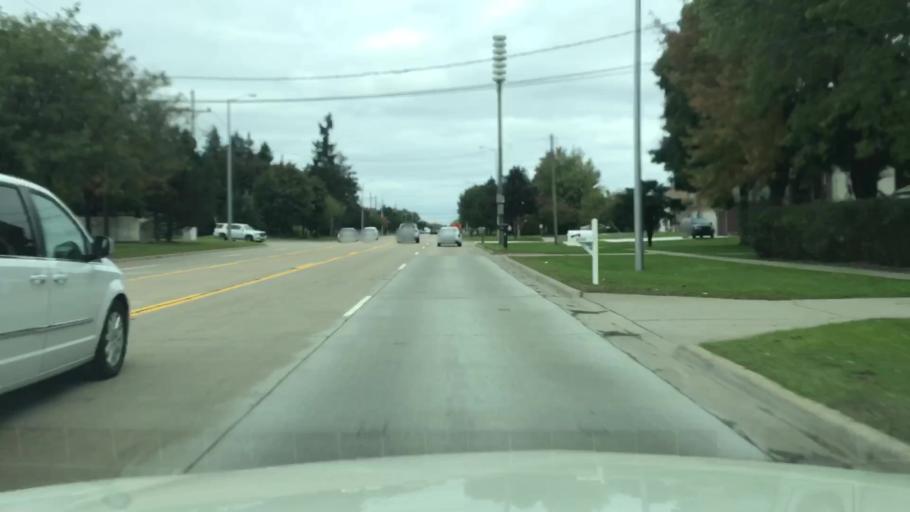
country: US
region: Michigan
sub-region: Macomb County
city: Sterling Heights
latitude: 42.5868
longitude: -83.0705
